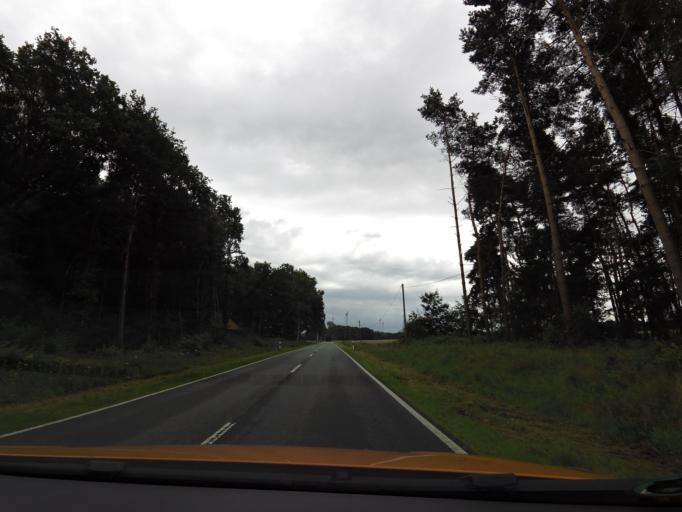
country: DE
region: Lower Saxony
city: Dunsen
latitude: 52.8827
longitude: 8.6316
